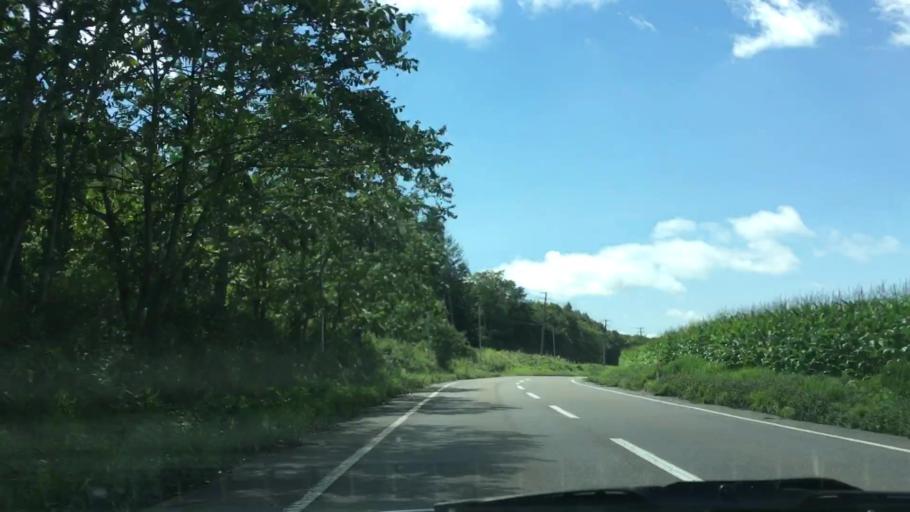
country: JP
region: Hokkaido
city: Kitami
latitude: 43.3244
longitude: 143.7313
